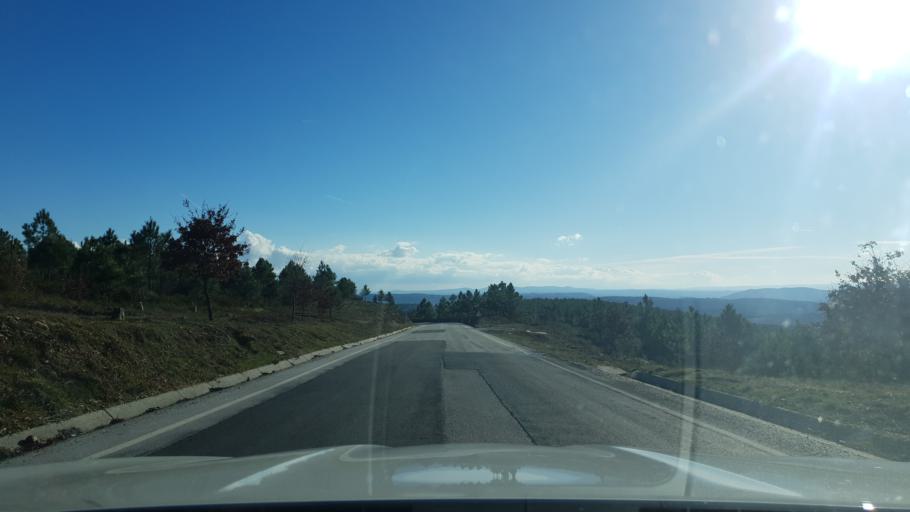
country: PT
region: Braganca
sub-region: Freixo de Espada A Cinta
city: Freixo de Espada a Cinta
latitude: 41.1426
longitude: -6.8079
